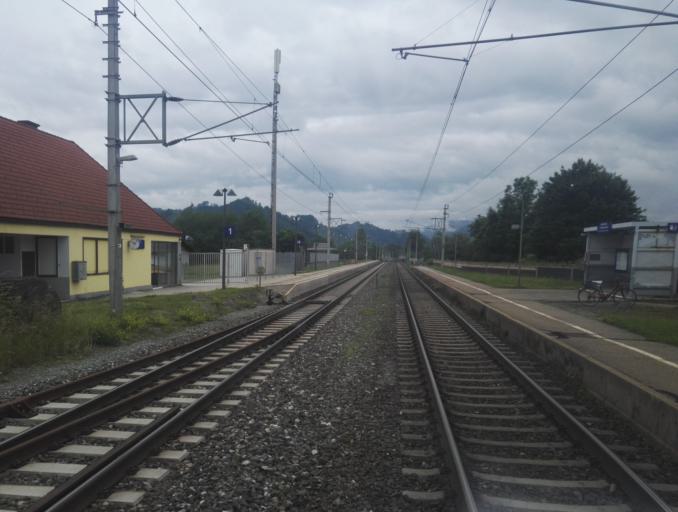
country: AT
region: Styria
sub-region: Politischer Bezirk Bruck-Muerzzuschlag
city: Frauenberg
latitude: 47.4549
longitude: 15.3296
